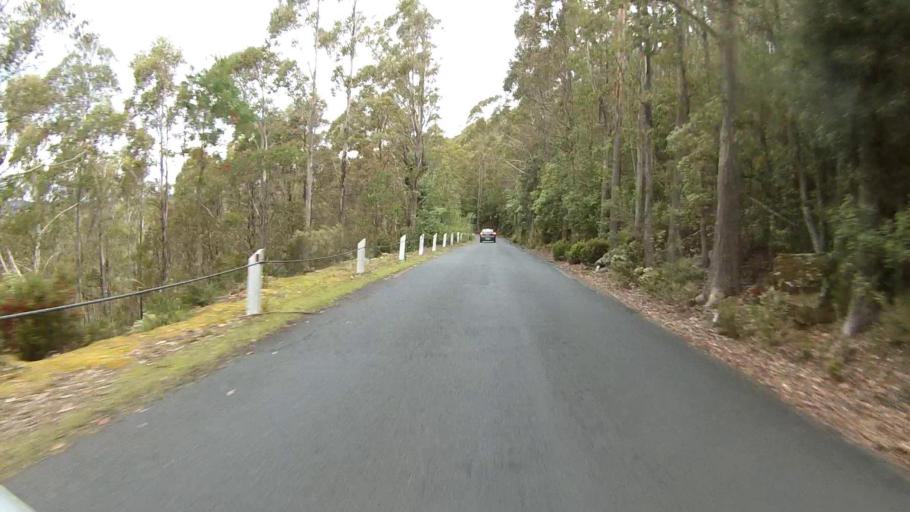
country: AU
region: Tasmania
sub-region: Glenorchy
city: West Moonah
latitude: -42.9107
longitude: 147.2440
